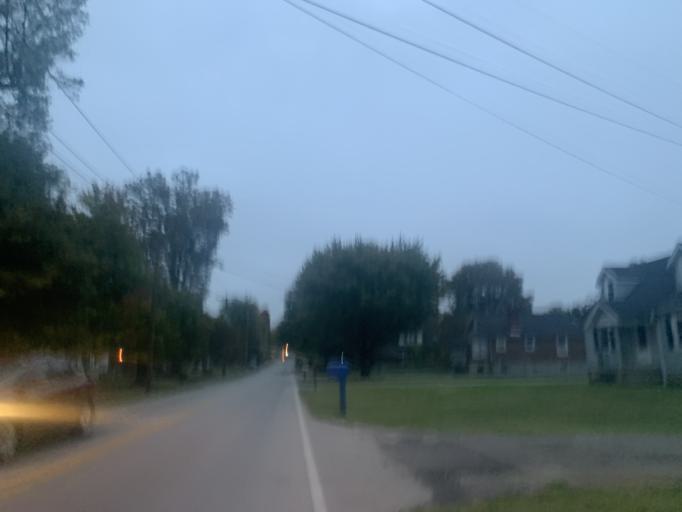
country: US
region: Kentucky
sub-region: Jefferson County
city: Shively
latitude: 38.2150
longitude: -85.7995
